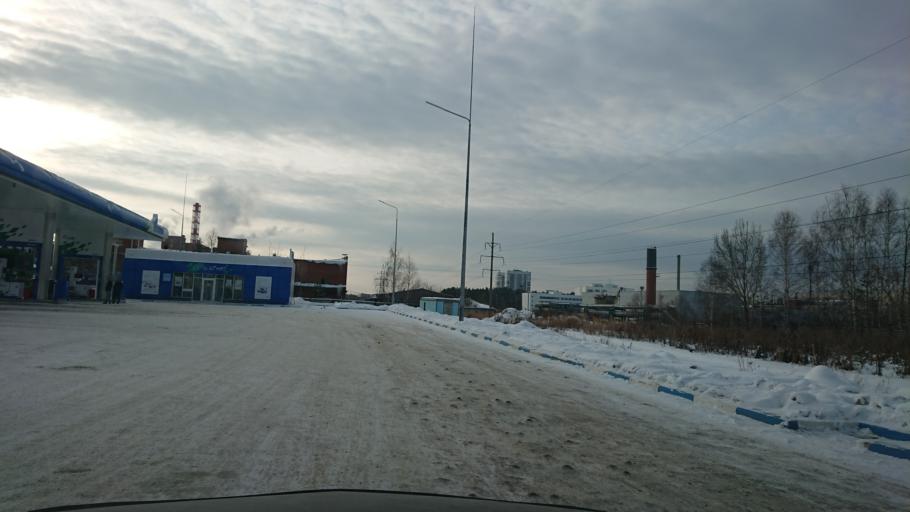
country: RU
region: Sverdlovsk
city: Sovkhoznyy
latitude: 56.7777
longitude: 60.5604
